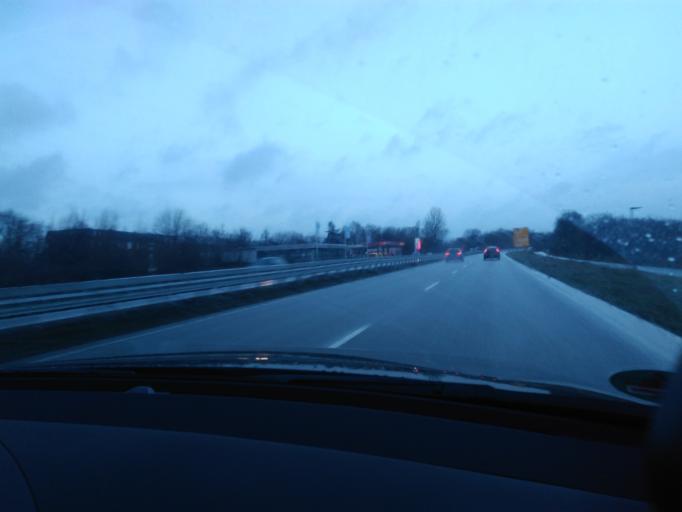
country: DE
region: Schleswig-Holstein
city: Altenholz
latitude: 54.3796
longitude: 10.1335
